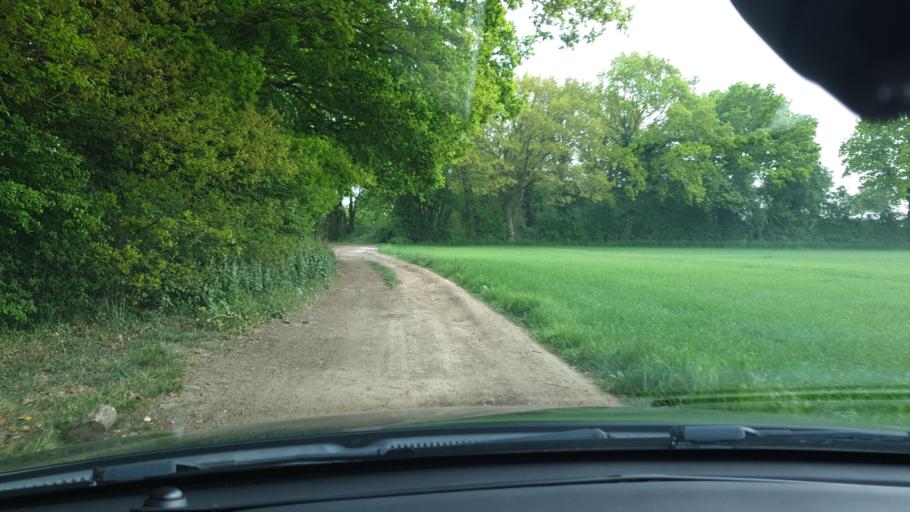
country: GB
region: England
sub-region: Essex
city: Little Clacton
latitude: 51.8359
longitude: 1.1458
